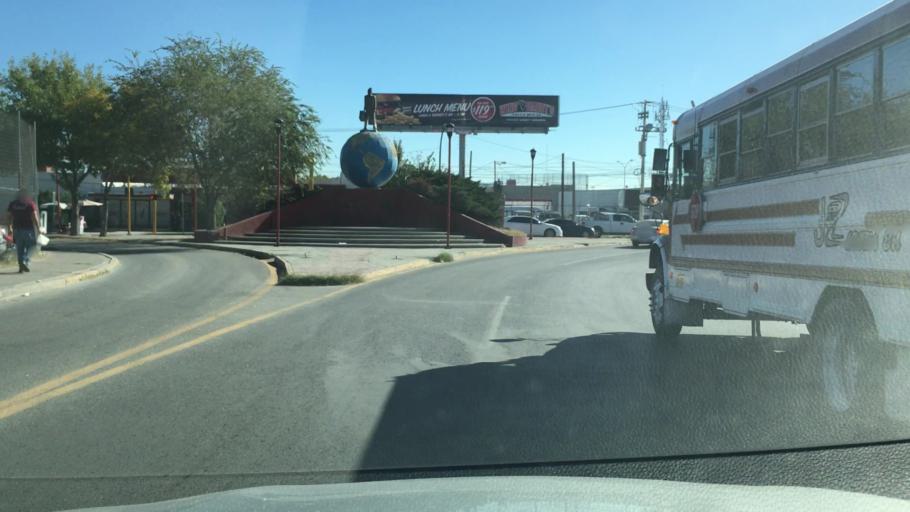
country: MX
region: Chihuahua
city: Ciudad Juarez
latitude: 31.7387
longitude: -106.4500
